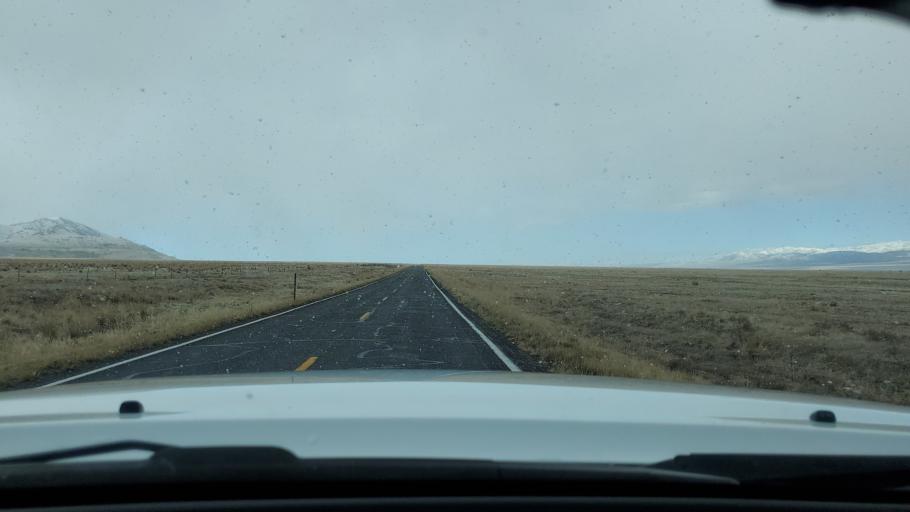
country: US
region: Utah
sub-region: Tooele County
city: Grantsville
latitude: 40.6046
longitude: -112.7093
